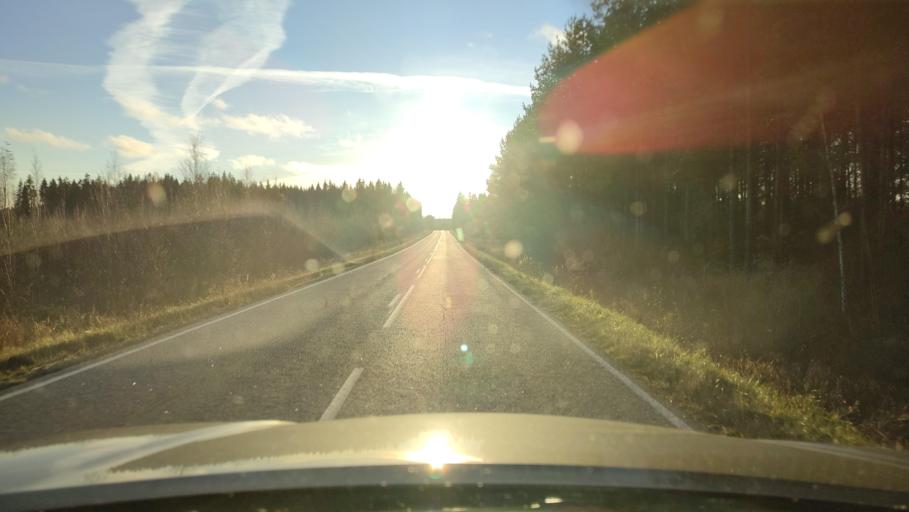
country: FI
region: Ostrobothnia
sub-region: Vaasa
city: Malax
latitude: 62.6940
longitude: 21.5637
